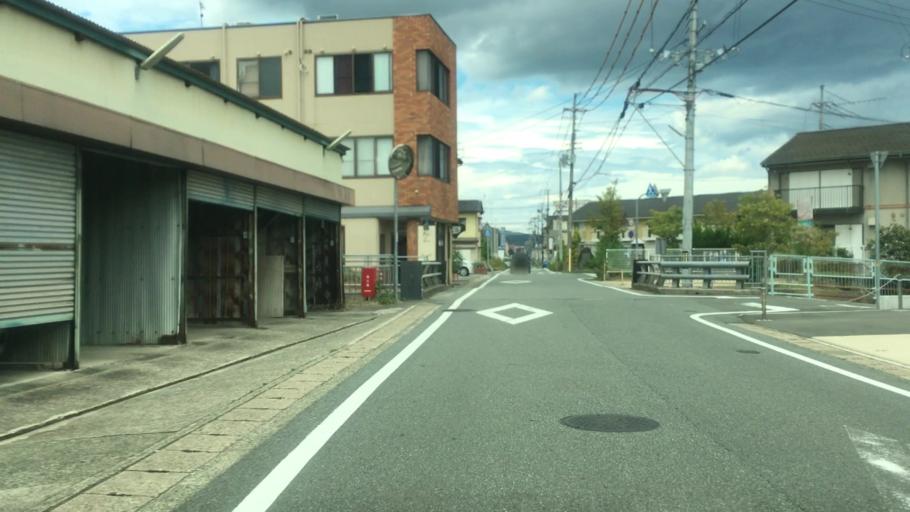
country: JP
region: Hyogo
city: Toyooka
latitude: 35.5317
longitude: 134.8211
